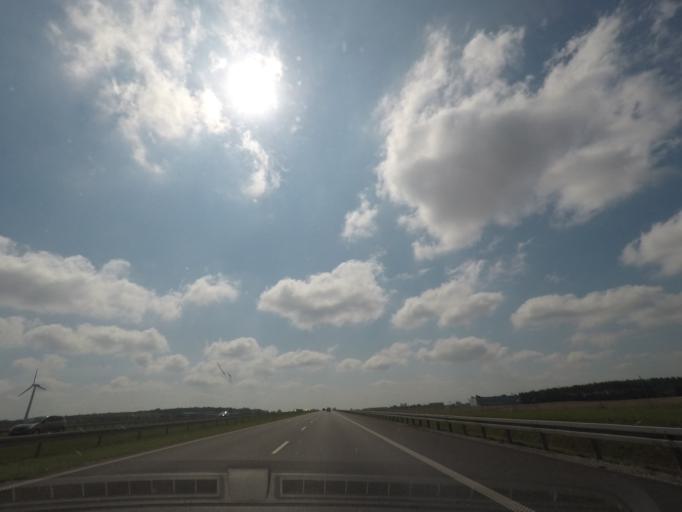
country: PL
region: Kujawsko-Pomorskie
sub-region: Powiat wloclawski
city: Brzesc Kujawski
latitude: 52.6424
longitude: 18.9462
